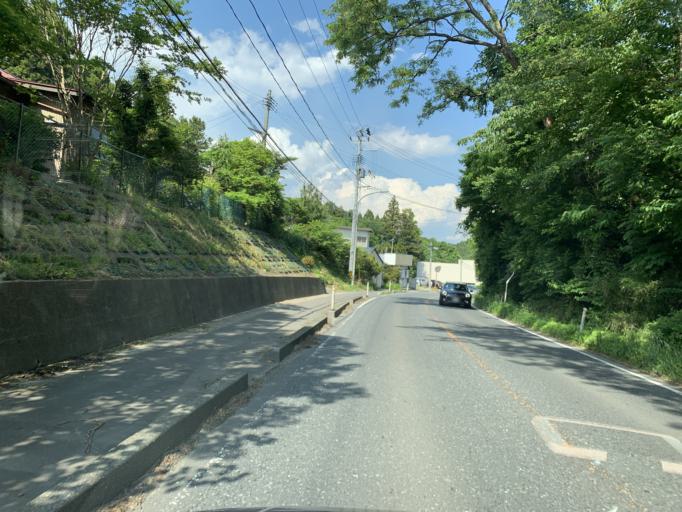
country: JP
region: Miyagi
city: Wakuya
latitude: 38.4911
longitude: 141.1095
